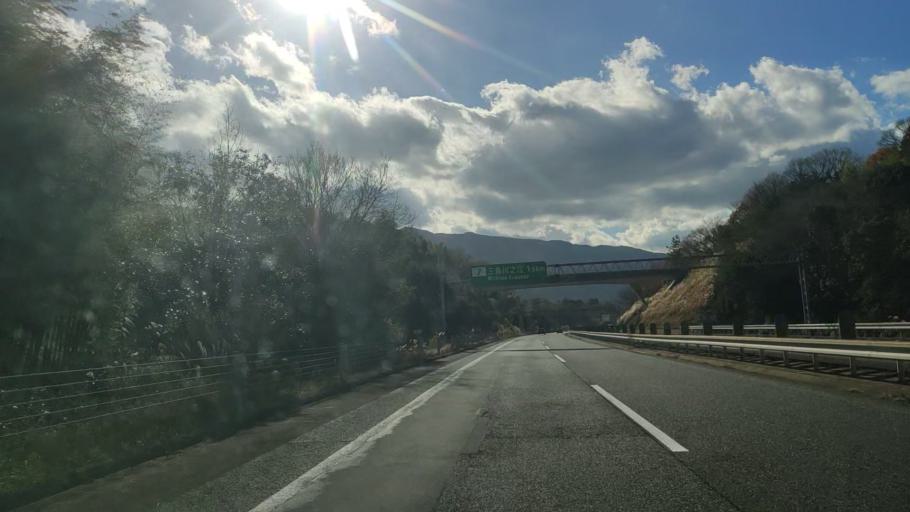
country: JP
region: Ehime
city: Kawanoecho
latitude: 33.9877
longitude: 133.5913
